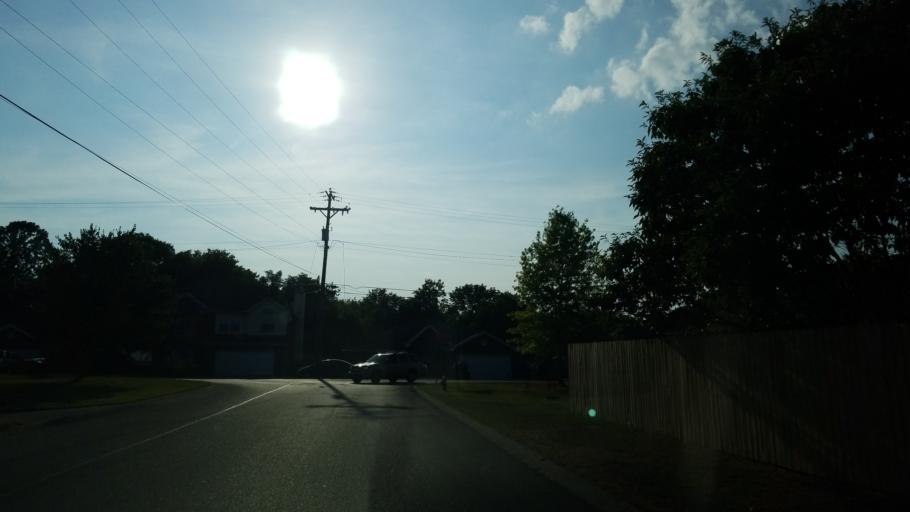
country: US
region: Tennessee
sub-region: Rutherford County
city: La Vergne
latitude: 36.0308
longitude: -86.5834
